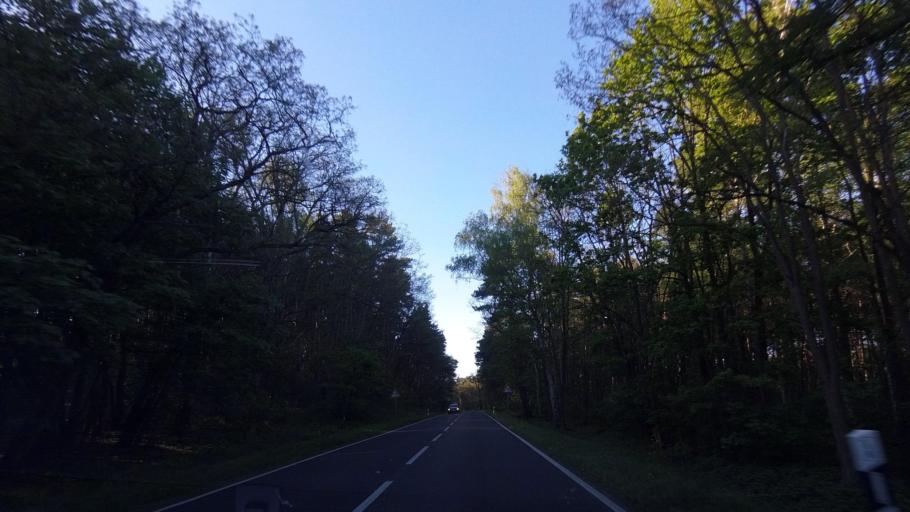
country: DE
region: Brandenburg
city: Golssen
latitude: 51.9990
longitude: 13.5590
